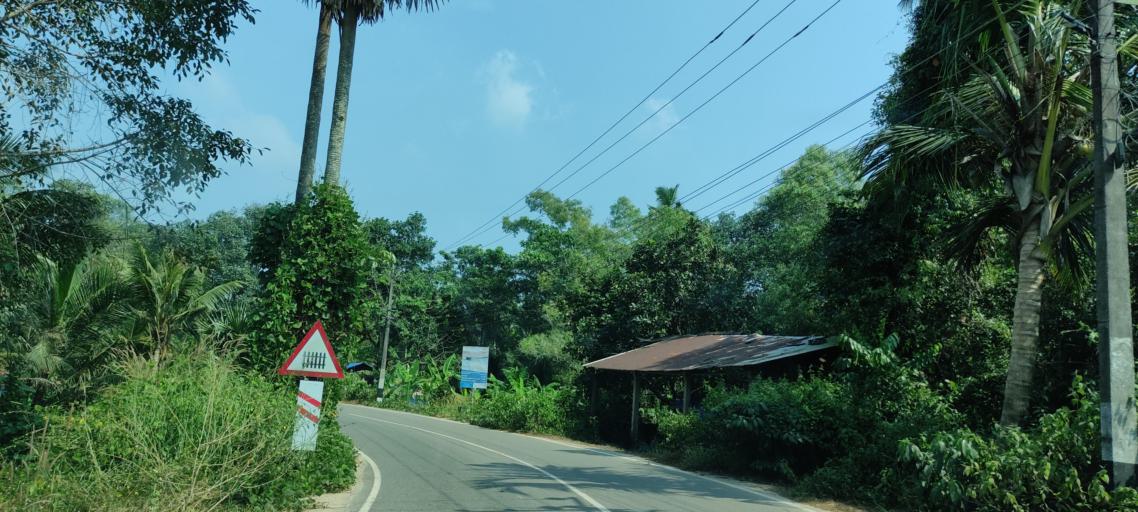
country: IN
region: Kerala
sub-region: Alappuzha
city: Shertallai
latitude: 9.6011
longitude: 76.3169
